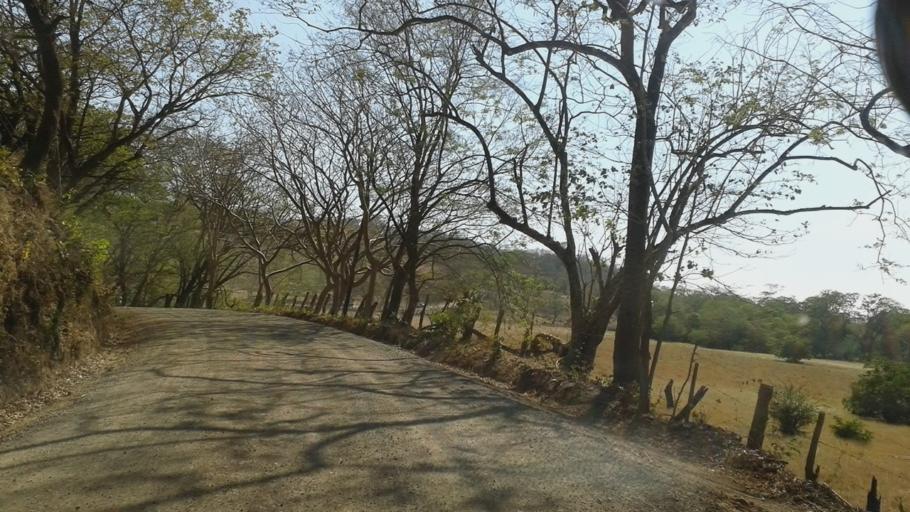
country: CR
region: Guanacaste
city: Santa Cruz
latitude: 10.1861
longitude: -85.7688
